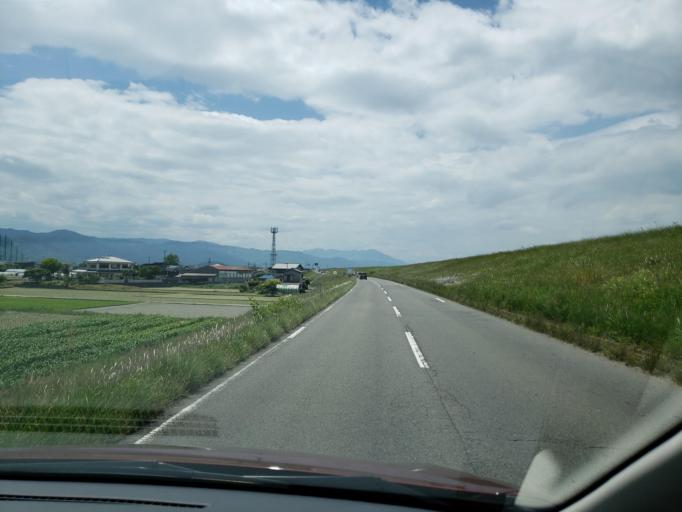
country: JP
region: Tokushima
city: Ishii
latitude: 34.1002
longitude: 134.4293
